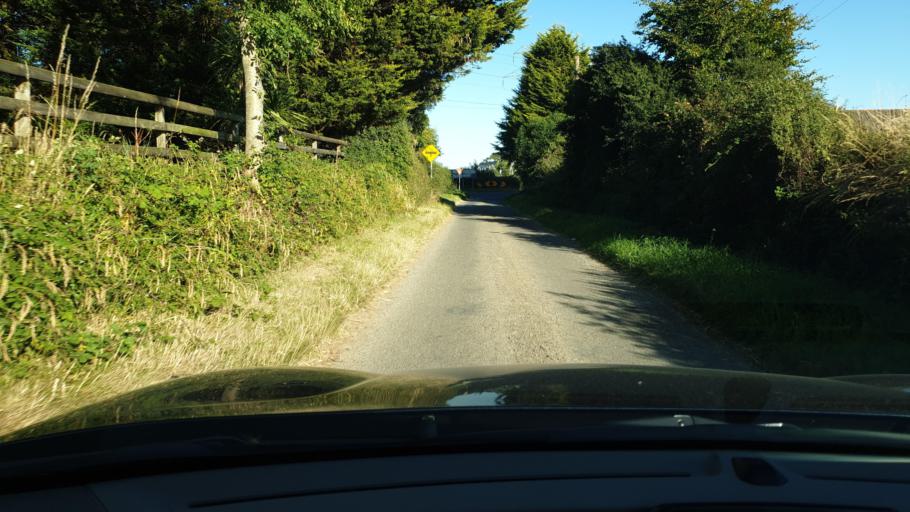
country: IE
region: Leinster
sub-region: Fingal County
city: Blanchardstown
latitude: 53.4366
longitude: -6.3580
